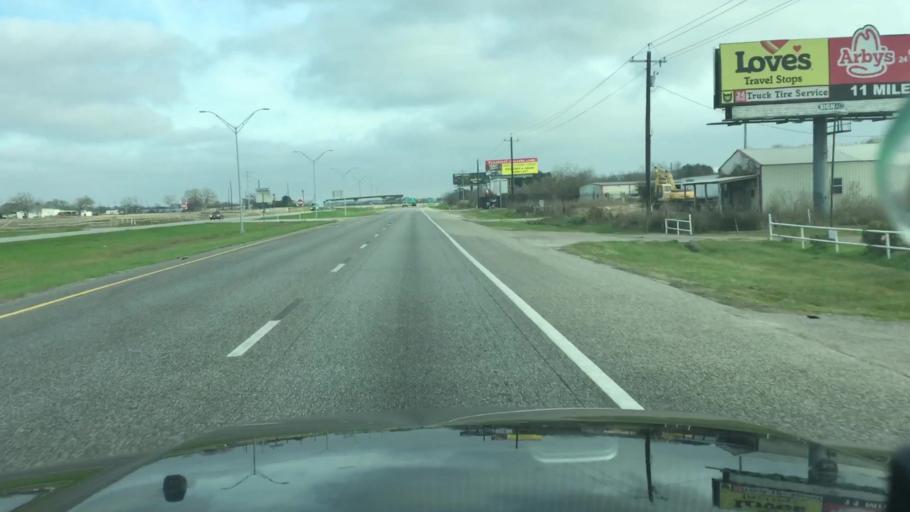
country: US
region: Texas
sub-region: Waller County
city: Hempstead
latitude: 30.1171
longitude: -96.0879
